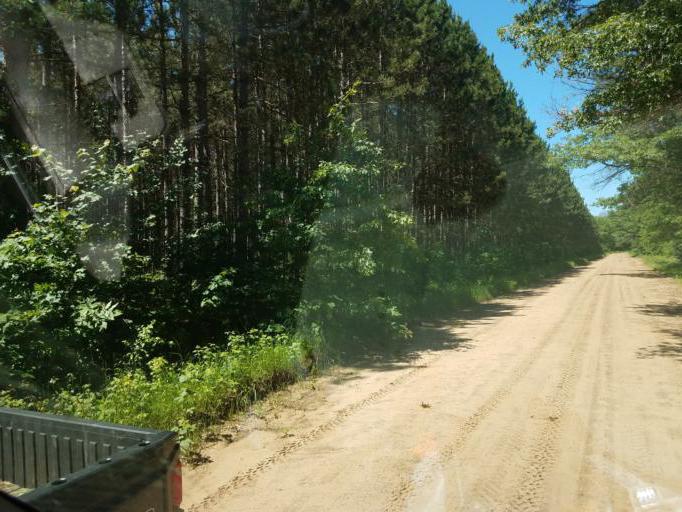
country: US
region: Wisconsin
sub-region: Adams County
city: Friendship
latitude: 44.0249
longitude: -89.9870
